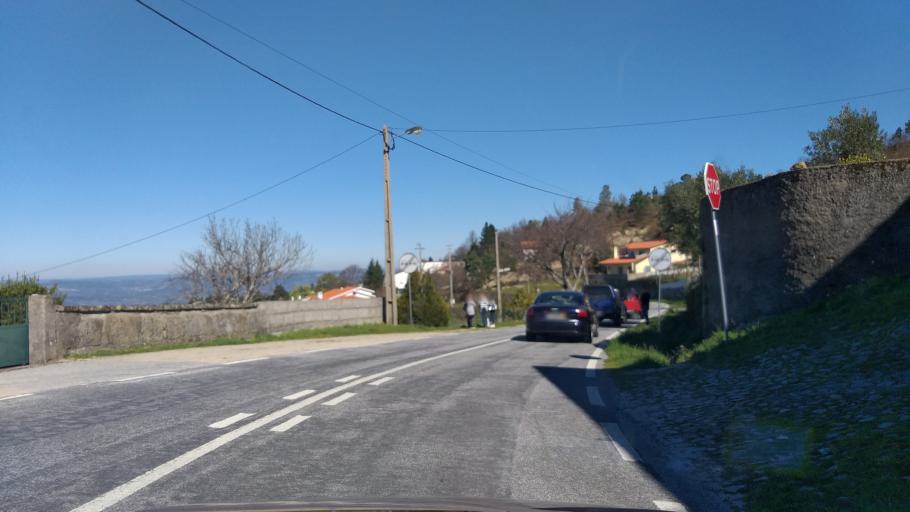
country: PT
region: Guarda
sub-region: Manteigas
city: Manteigas
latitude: 40.4792
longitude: -7.5961
